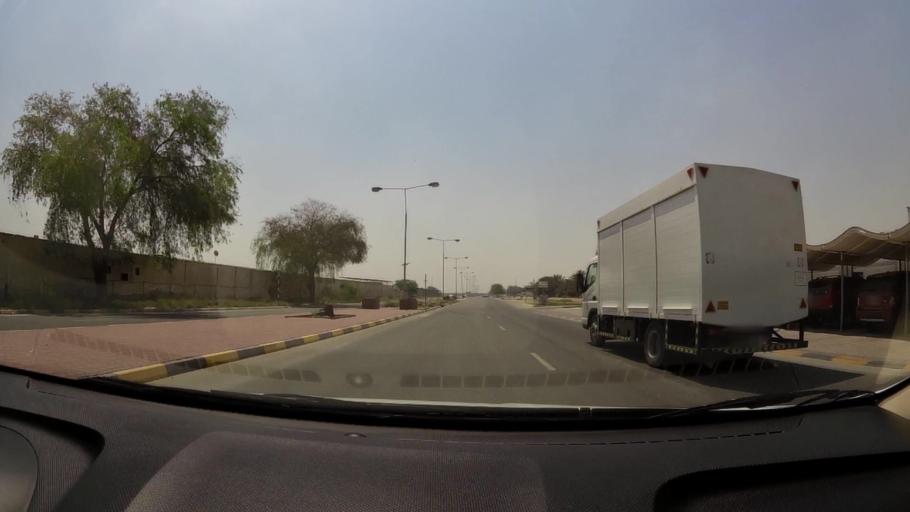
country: AE
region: Umm al Qaywayn
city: Umm al Qaywayn
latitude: 25.5640
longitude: 55.5565
